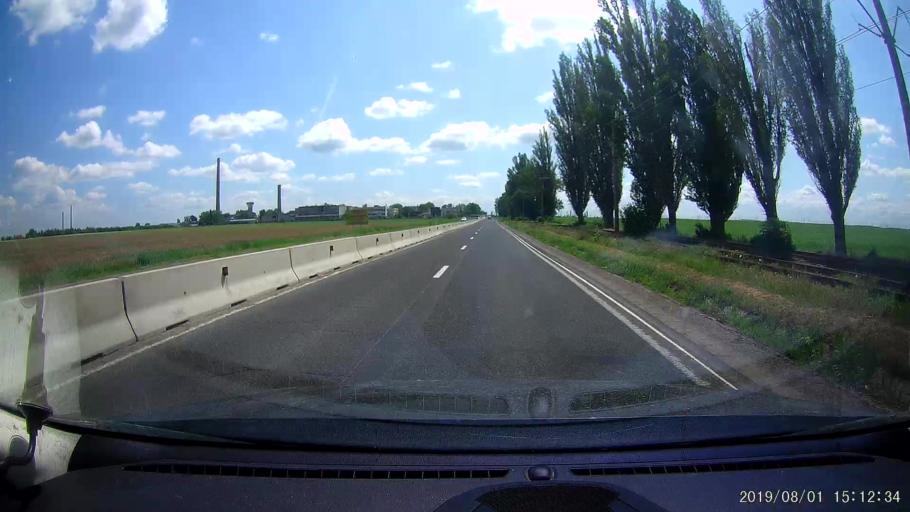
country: RO
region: Braila
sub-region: Comuna Chiscani
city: Lacu Sarat
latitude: 45.2049
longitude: 27.9121
